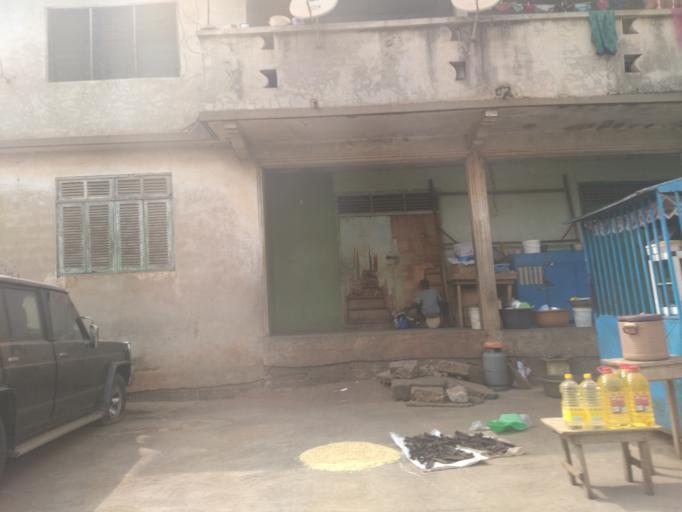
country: GH
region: Ashanti
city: Tafo
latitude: 6.7134
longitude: -1.6121
